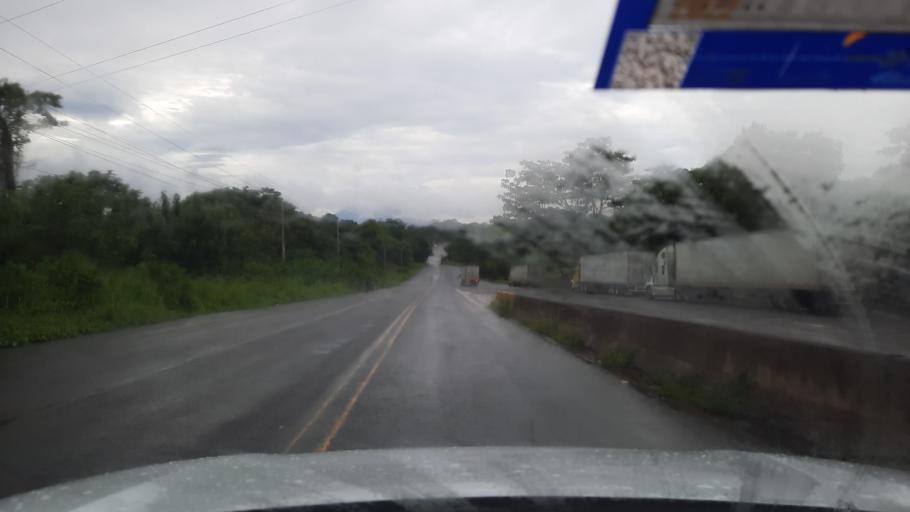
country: NI
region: Rivas
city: Cardenas
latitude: 11.1992
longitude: -85.6197
